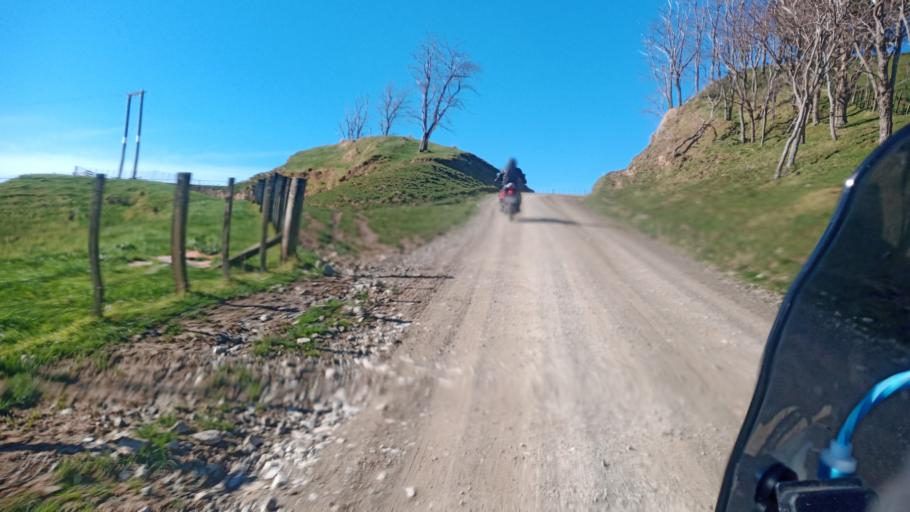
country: NZ
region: Gisborne
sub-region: Gisborne District
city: Gisborne
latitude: -38.2942
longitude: 177.8939
